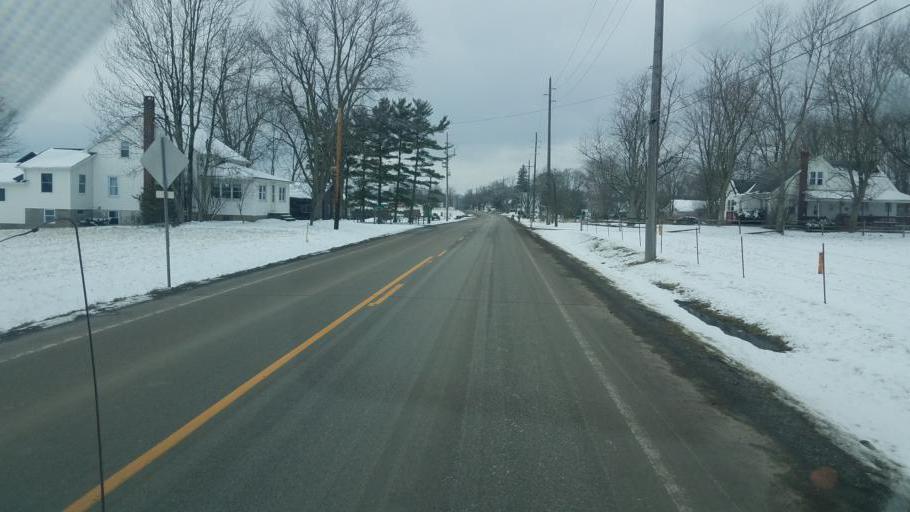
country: US
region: Ohio
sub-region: Geauga County
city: Middlefield
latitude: 41.4494
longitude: -81.0738
